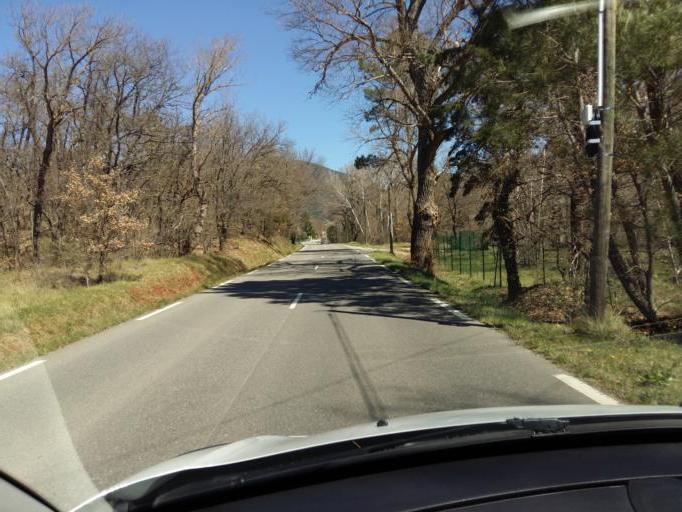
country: FR
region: Provence-Alpes-Cote d'Azur
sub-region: Departement du Vaucluse
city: Apt
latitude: 43.9115
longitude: 5.4436
